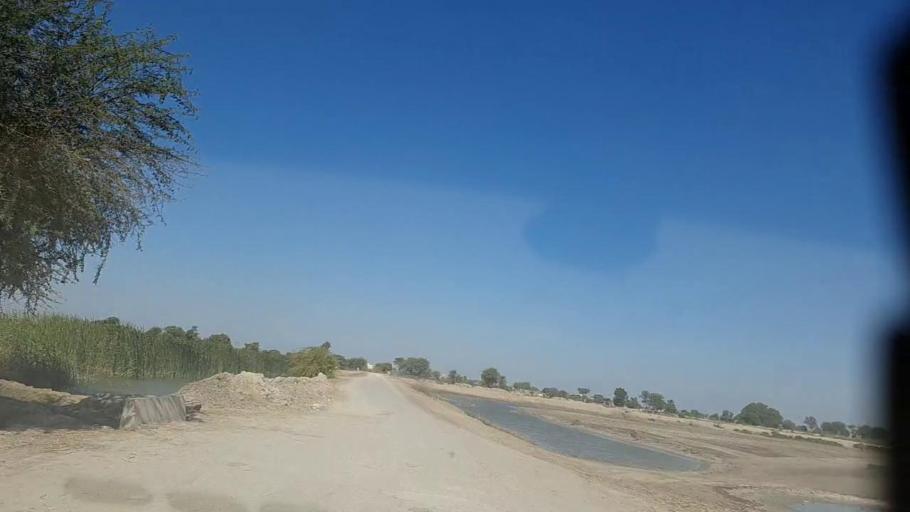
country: PK
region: Sindh
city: Digri
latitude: 25.1767
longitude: 69.0486
